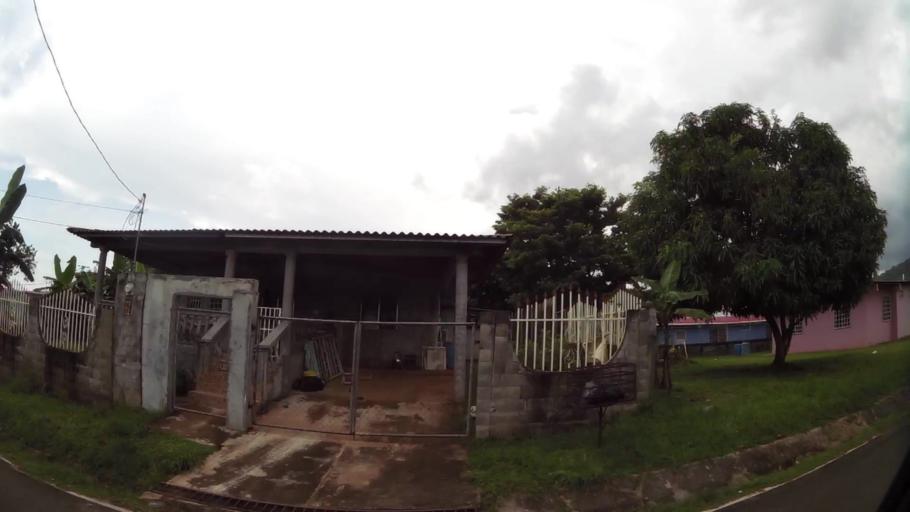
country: PA
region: Panama
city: Tocumen
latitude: 9.1108
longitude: -79.3757
